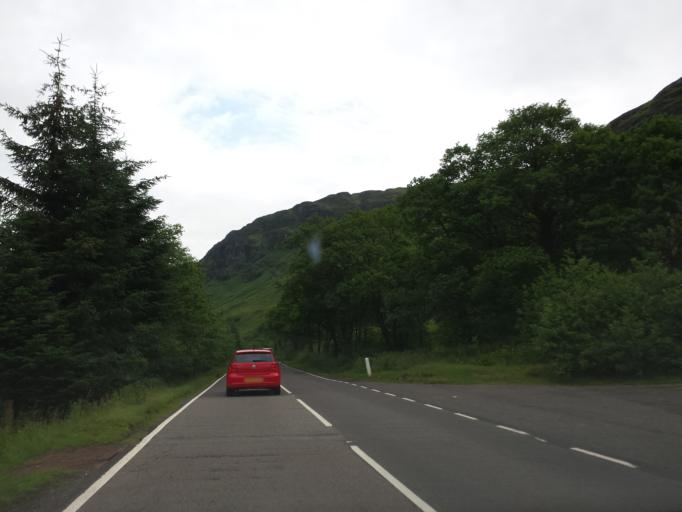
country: GB
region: Scotland
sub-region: Stirling
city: Callander
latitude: 56.4019
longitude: -4.3033
